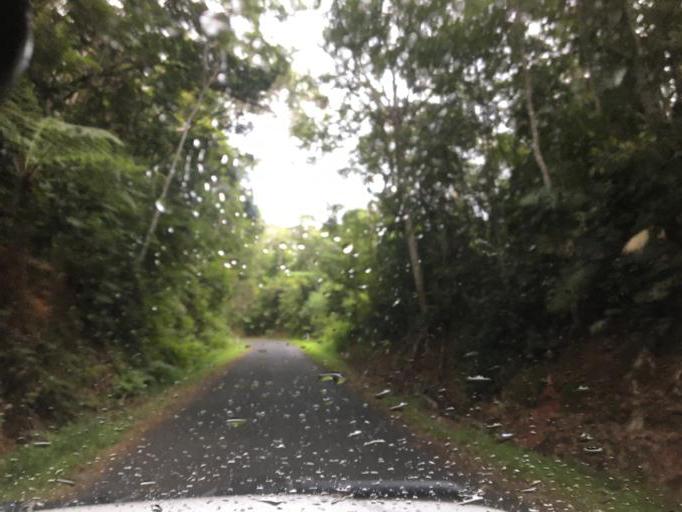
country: AU
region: Queensland
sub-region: Tablelands
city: Kuranda
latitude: -16.8413
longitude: 145.6423
